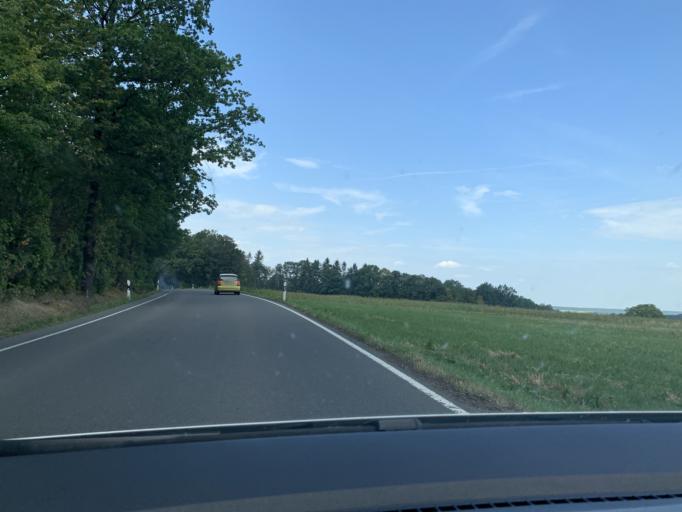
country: DE
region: Saxony
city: Falkenau
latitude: 50.9072
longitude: 13.1097
